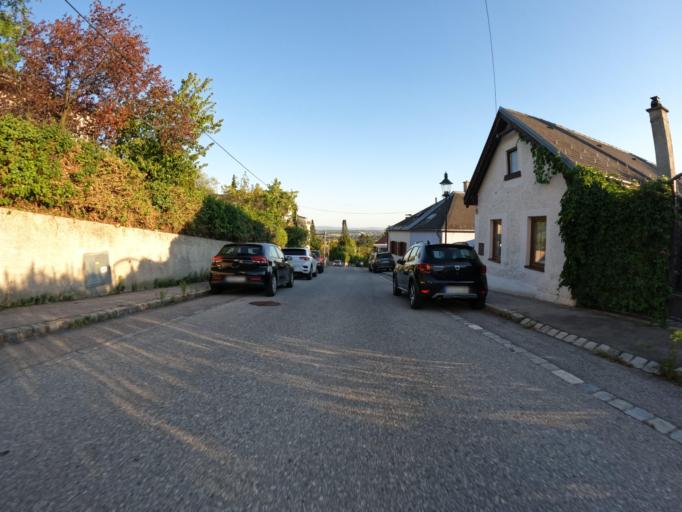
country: AT
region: Lower Austria
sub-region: Politischer Bezirk Baden
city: Baden
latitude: 48.0137
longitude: 16.2253
